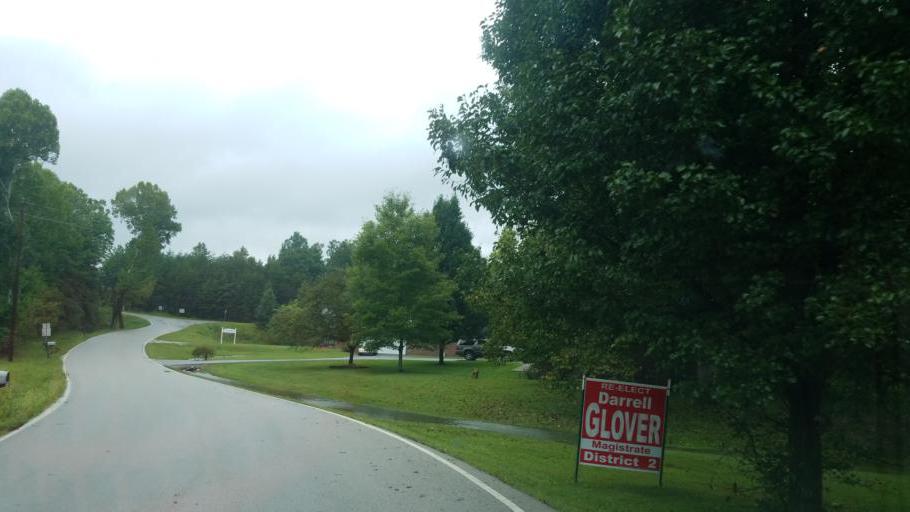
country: US
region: Kentucky
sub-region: Rowan County
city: Morehead
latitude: 38.1494
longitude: -83.5062
